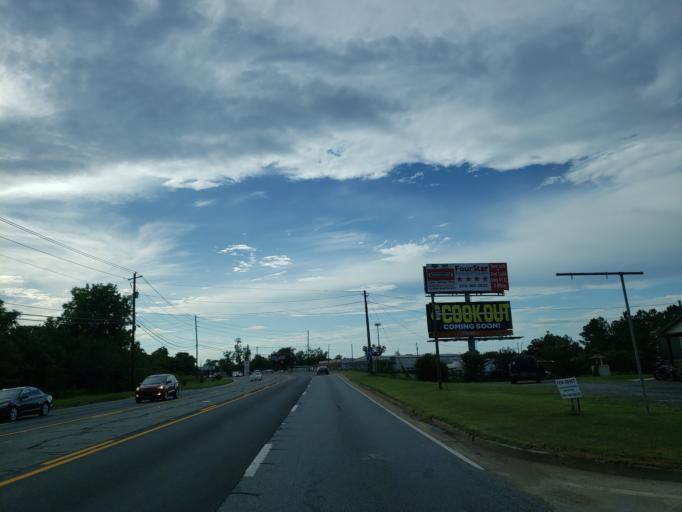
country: US
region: Georgia
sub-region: Tift County
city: Tifton
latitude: 31.4474
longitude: -83.4906
